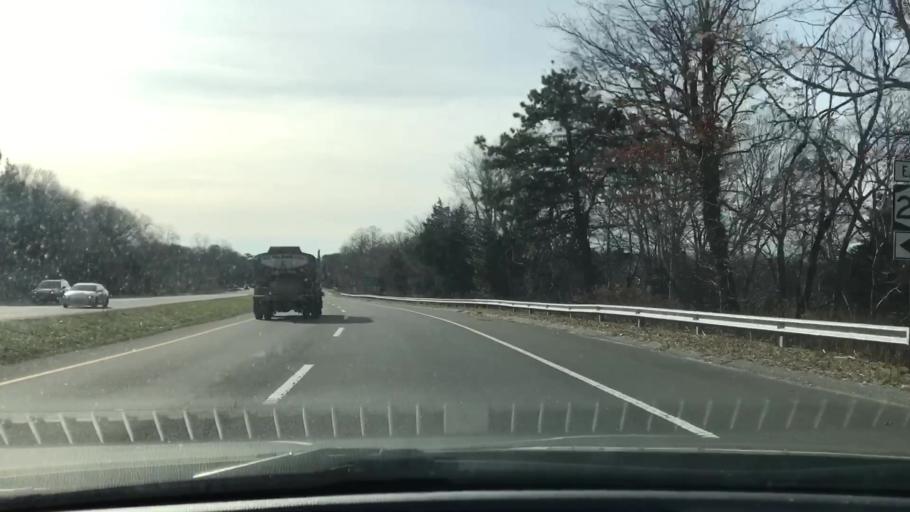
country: US
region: New York
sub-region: Suffolk County
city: Riverhead
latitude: 40.9139
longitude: -72.6412
